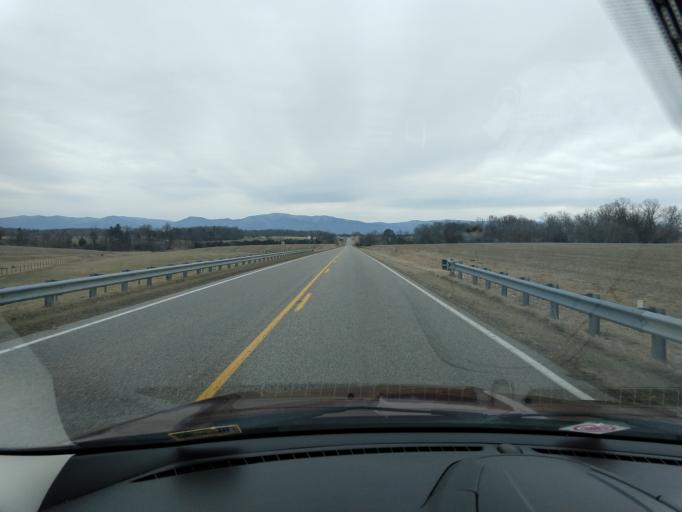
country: US
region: Virginia
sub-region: Augusta County
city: Weyers Cave
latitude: 38.2791
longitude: -78.8997
